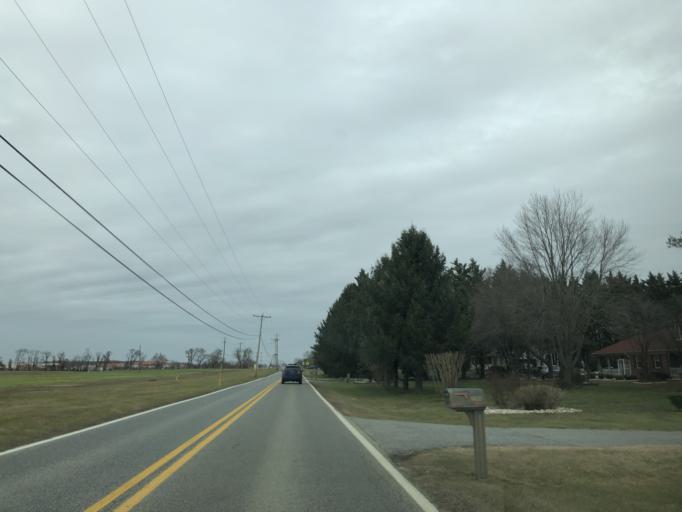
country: US
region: Delaware
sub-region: New Castle County
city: Middletown
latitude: 39.4950
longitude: -75.6883
